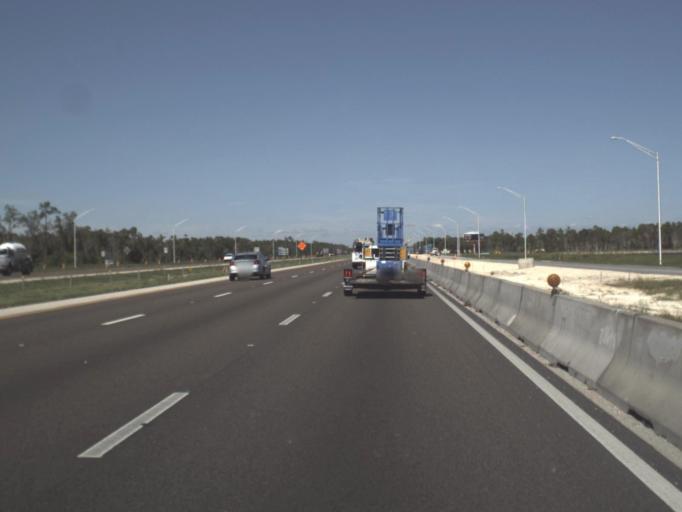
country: US
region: Florida
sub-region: Lee County
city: Three Oaks
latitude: 26.5194
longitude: -81.7945
